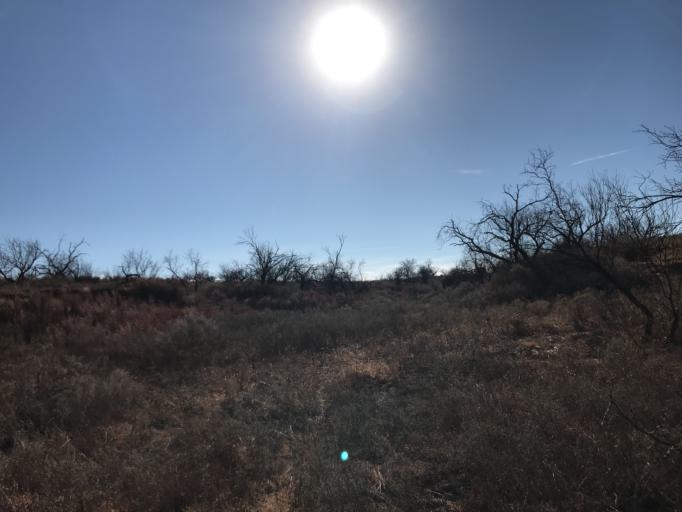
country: US
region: Texas
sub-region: Childress County
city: Childress
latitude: 34.3250
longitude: -100.4745
